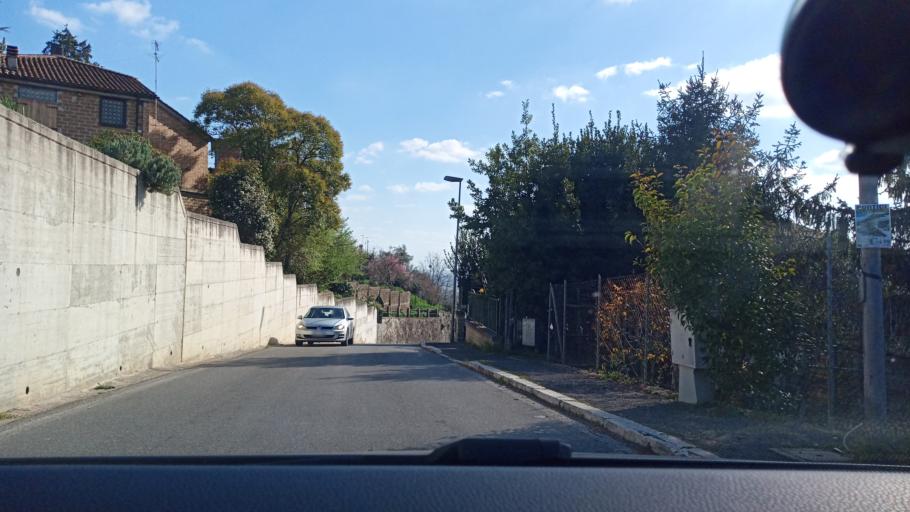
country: IT
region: Latium
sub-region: Citta metropolitana di Roma Capitale
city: Torrita Tiberina
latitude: 42.2396
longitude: 12.6155
